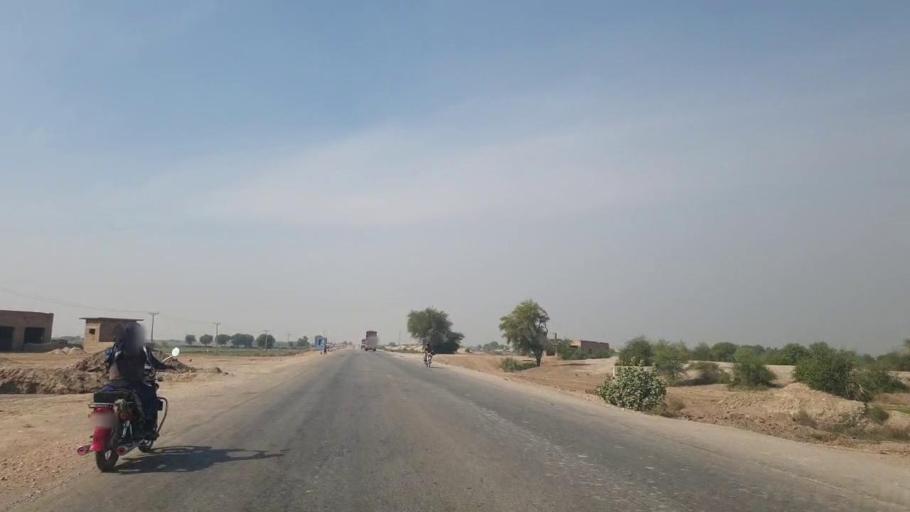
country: PK
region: Sindh
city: Sann
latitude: 25.9895
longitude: 68.1770
